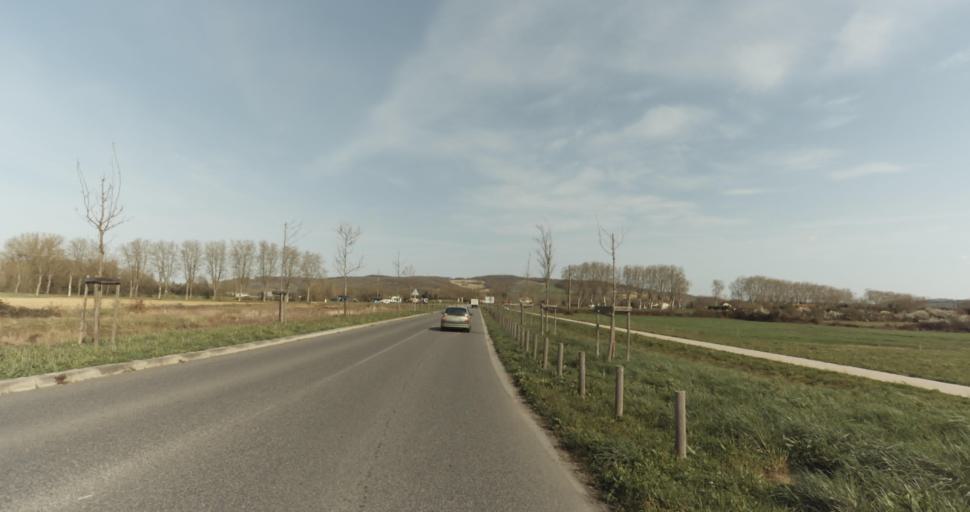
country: FR
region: Midi-Pyrenees
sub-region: Departement de la Haute-Garonne
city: Buzet-sur-Tarn
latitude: 43.7687
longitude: 1.6562
